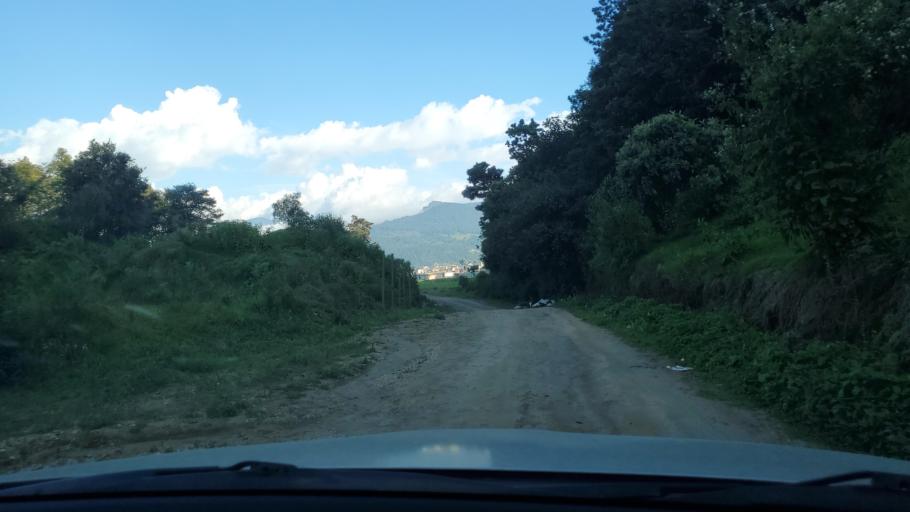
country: GT
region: Quetzaltenango
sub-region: Municipio de La Esperanza
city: La Esperanza
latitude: 14.8377
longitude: -91.5531
